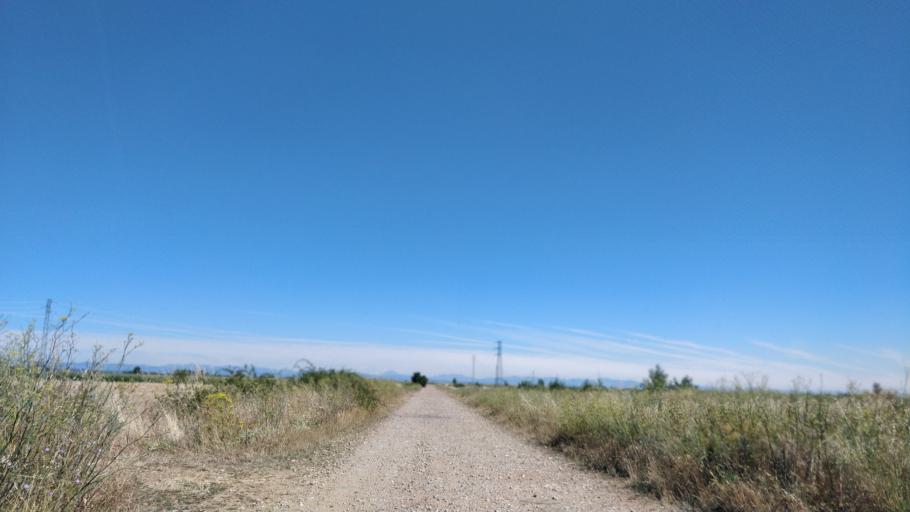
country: ES
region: Castille and Leon
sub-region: Provincia de Leon
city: Bustillo del Paramo
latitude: 42.4268
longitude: -5.8214
